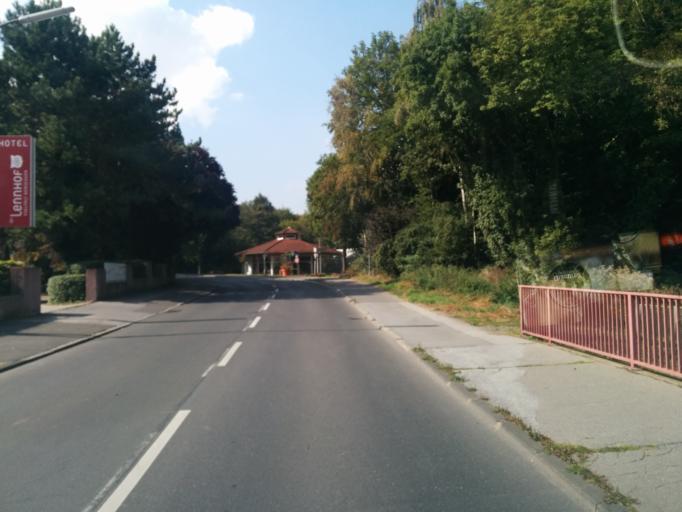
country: DE
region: North Rhine-Westphalia
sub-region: Regierungsbezirk Arnsberg
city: Dortmund
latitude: 51.4772
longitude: 7.4276
